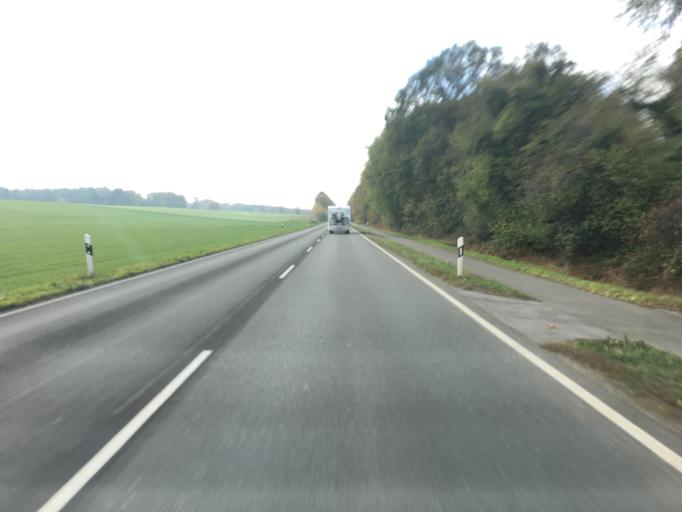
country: DE
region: North Rhine-Westphalia
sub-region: Regierungsbezirk Dusseldorf
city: Sonsbeck
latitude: 51.6318
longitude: 6.4033
